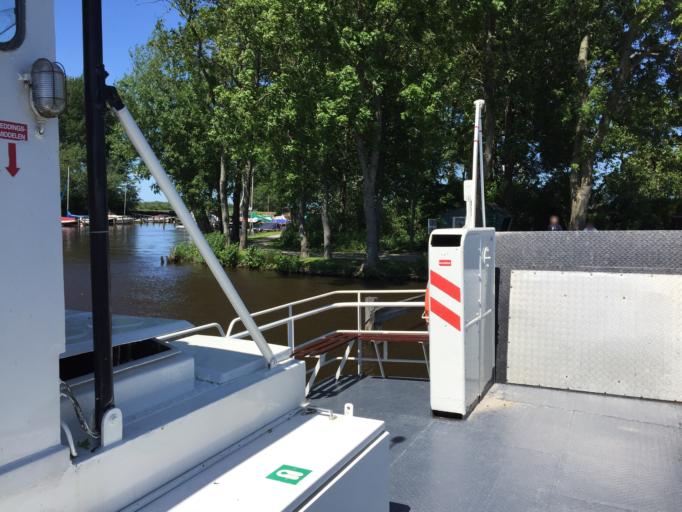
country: NL
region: Friesland
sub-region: Gemeente Smallingerland
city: Oudega
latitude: 53.1034
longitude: 5.9497
